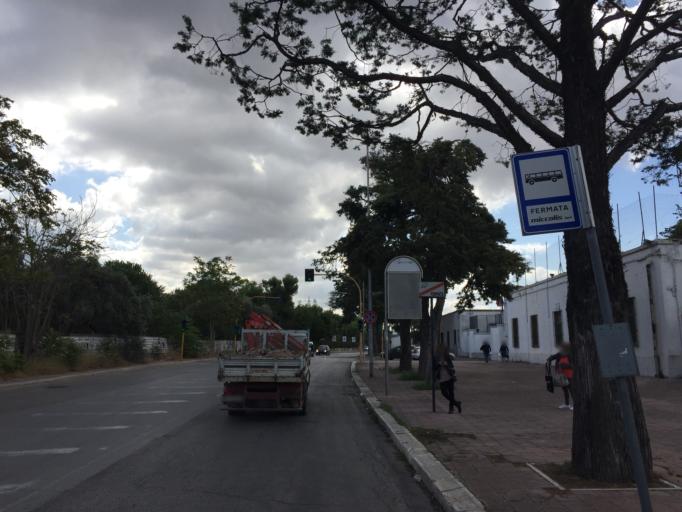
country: IT
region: Apulia
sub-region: Provincia di Bari
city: Bari
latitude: 41.0958
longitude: 16.8827
